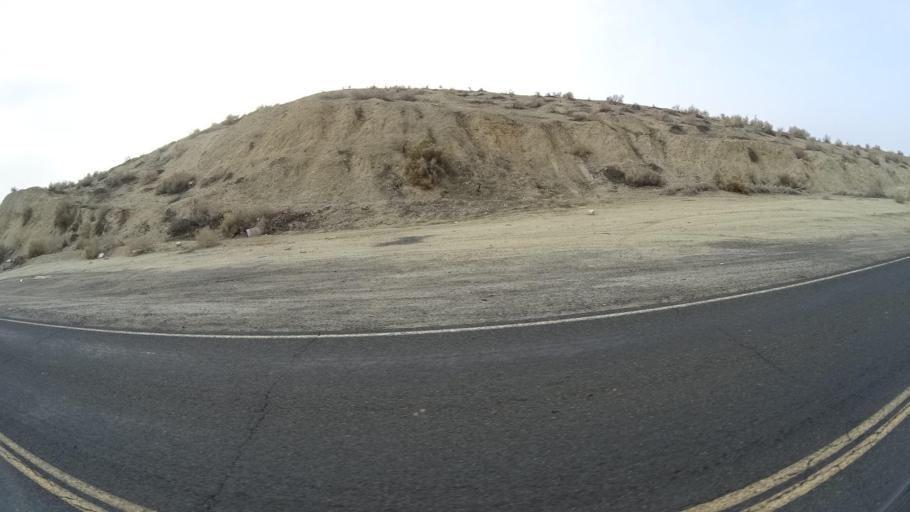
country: US
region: California
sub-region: Kern County
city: Ford City
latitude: 35.1916
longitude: -119.4456
